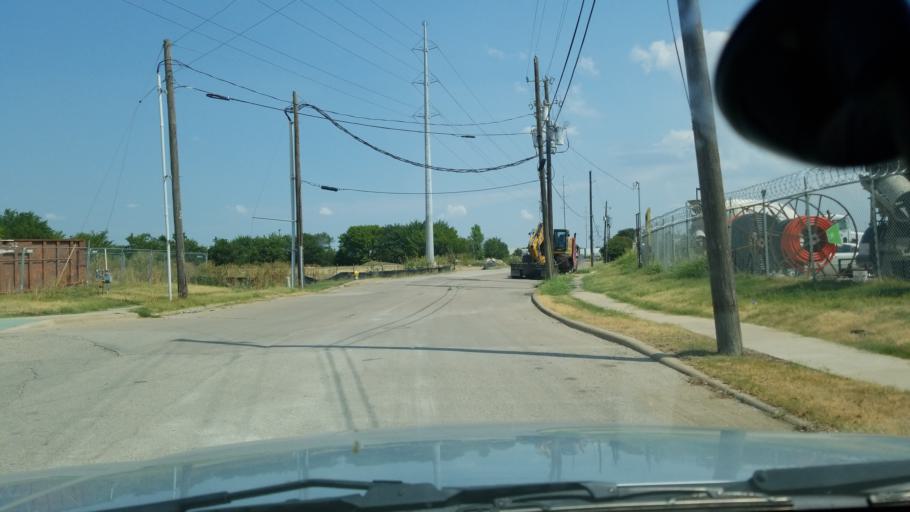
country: US
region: Texas
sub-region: Dallas County
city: Farmers Branch
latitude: 32.8690
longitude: -96.9053
